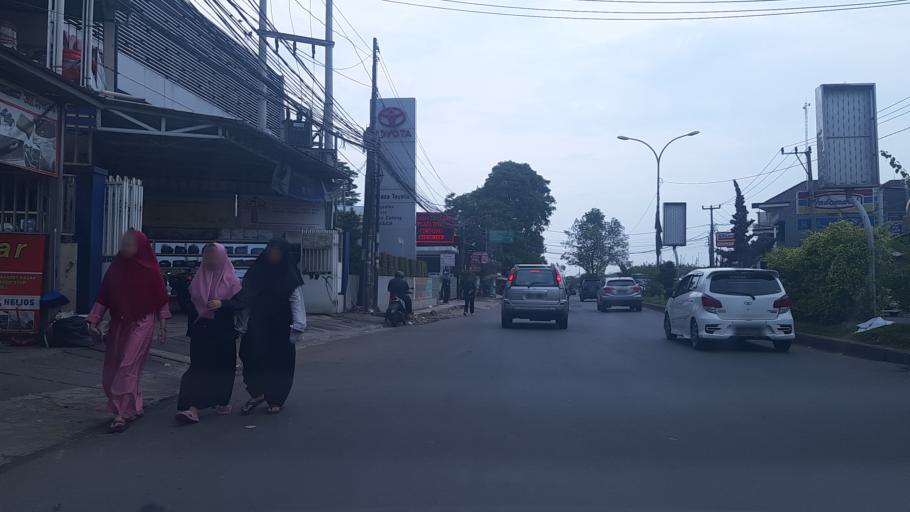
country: ID
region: West Java
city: Citeureup
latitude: -6.4841
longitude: 106.8705
